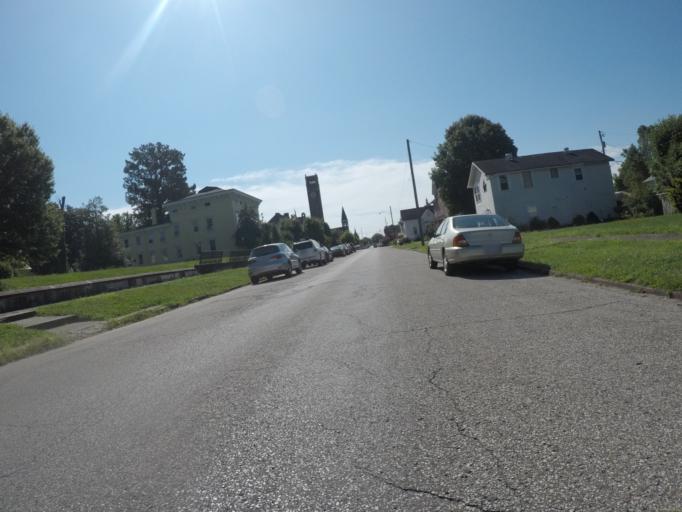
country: US
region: Ohio
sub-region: Lawrence County
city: Ironton
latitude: 38.5390
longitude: -82.6855
